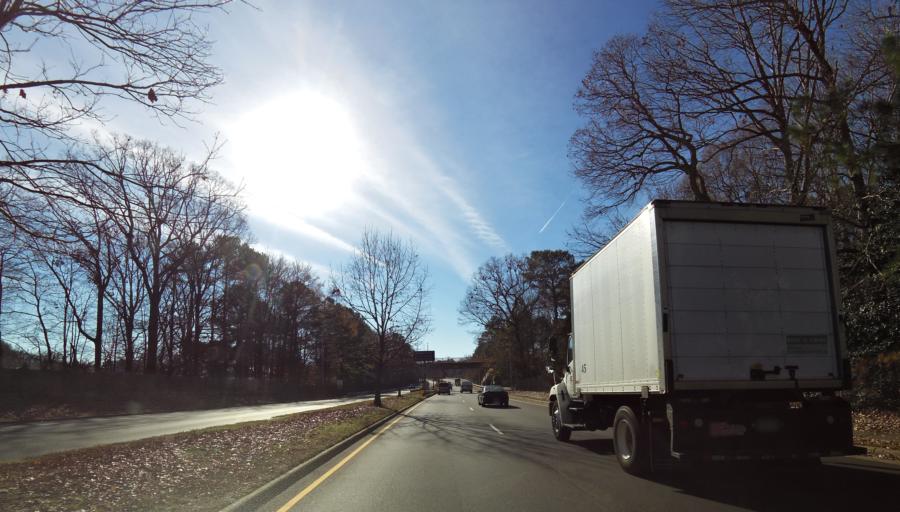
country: US
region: Virginia
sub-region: City of Hampton
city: Hampton
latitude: 37.0214
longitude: -76.3870
